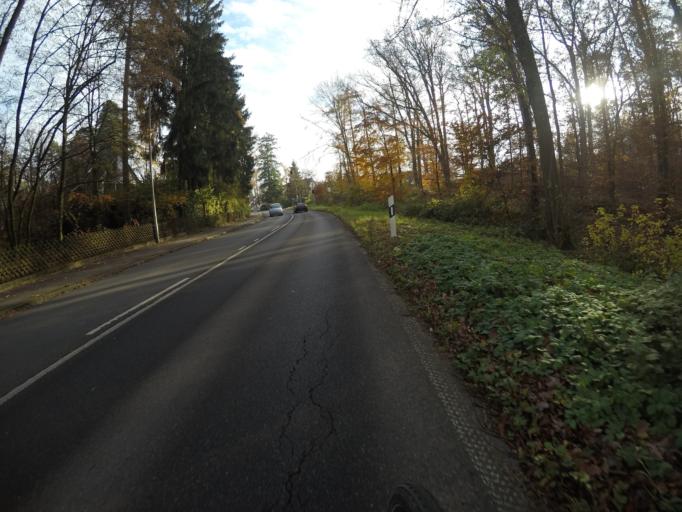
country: DE
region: Baden-Wuerttemberg
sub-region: Regierungsbezirk Stuttgart
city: Steinenbronn
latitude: 48.7073
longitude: 9.1101
